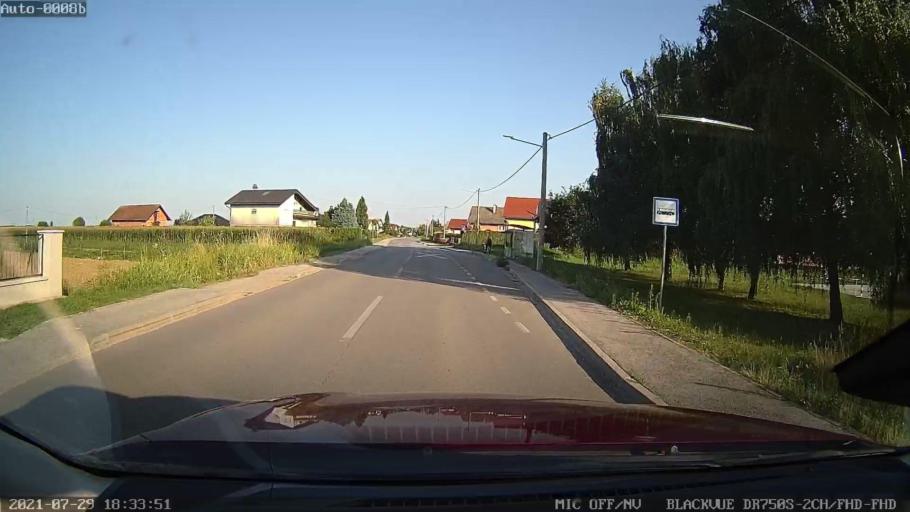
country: HR
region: Varazdinska
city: Vinica
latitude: 46.3134
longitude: 16.1612
